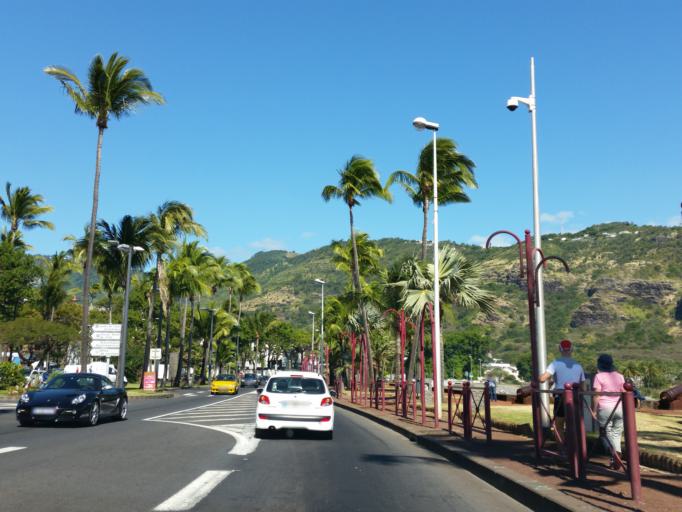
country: RE
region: Reunion
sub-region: Reunion
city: Saint-Denis
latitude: -20.8736
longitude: 55.4468
